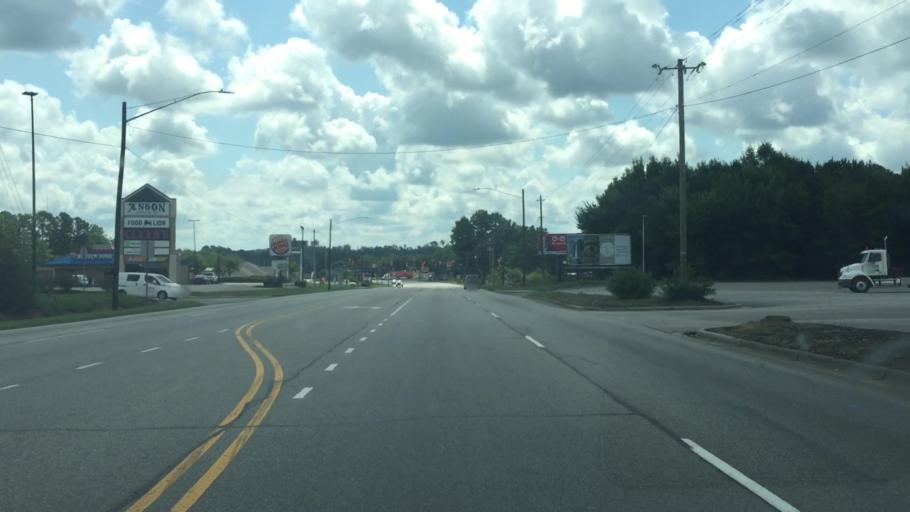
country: US
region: North Carolina
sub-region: Anson County
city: Wadesboro
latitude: 34.9662
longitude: -80.0618
